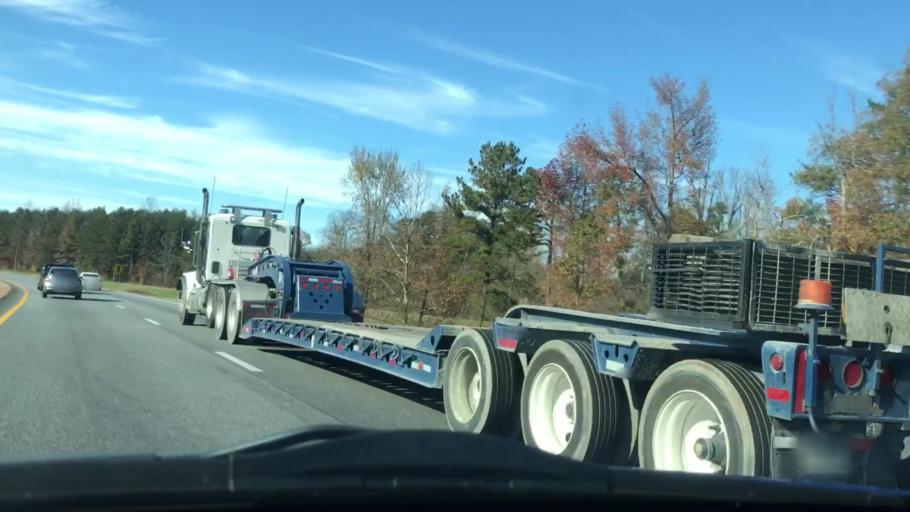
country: US
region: North Carolina
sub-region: Guilford County
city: High Point
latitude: 36.0136
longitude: -80.0371
